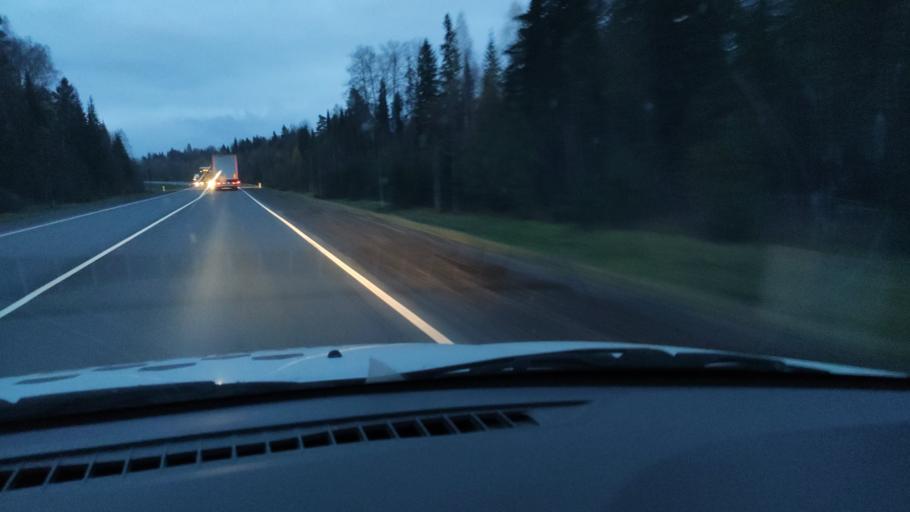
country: RU
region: Kirov
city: Kostino
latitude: 58.8276
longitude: 53.4199
